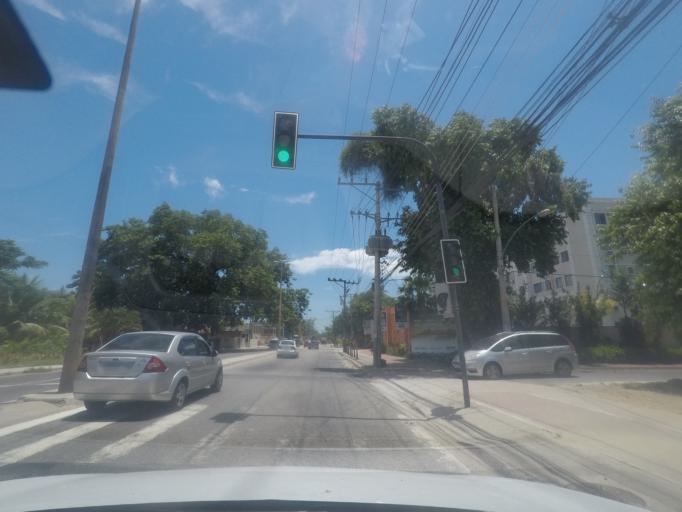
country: BR
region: Rio de Janeiro
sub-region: Itaguai
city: Itaguai
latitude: -22.8987
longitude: -43.6789
